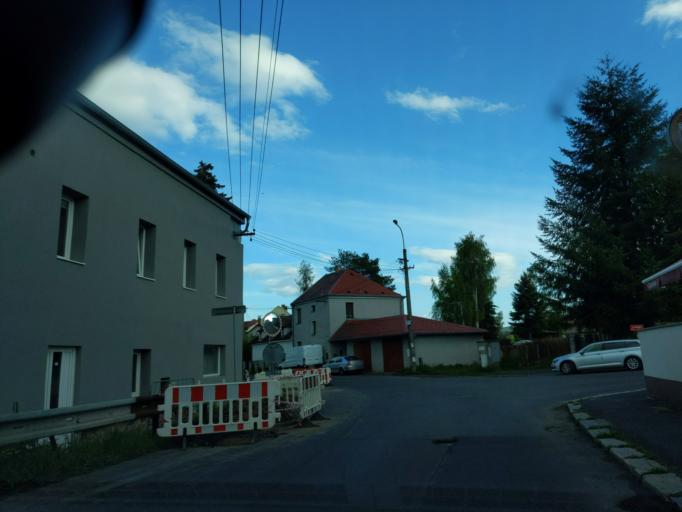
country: CZ
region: Ustecky
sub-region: Okres Usti nad Labem
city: Usti nad Labem
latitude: 50.6903
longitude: 14.0054
